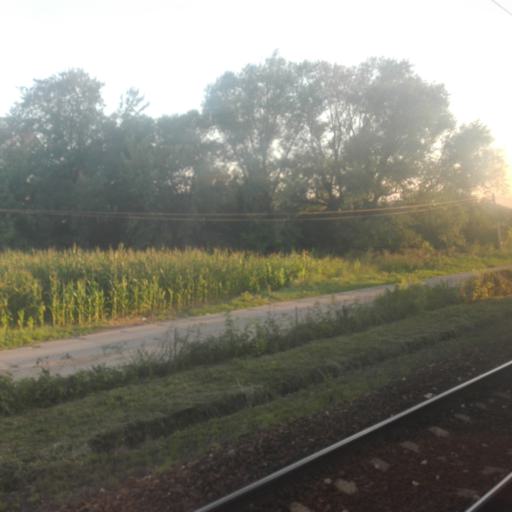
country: PL
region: Masovian Voivodeship
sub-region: Powiat warszawski zachodni
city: Bieniewice
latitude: 52.1860
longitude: 20.5755
